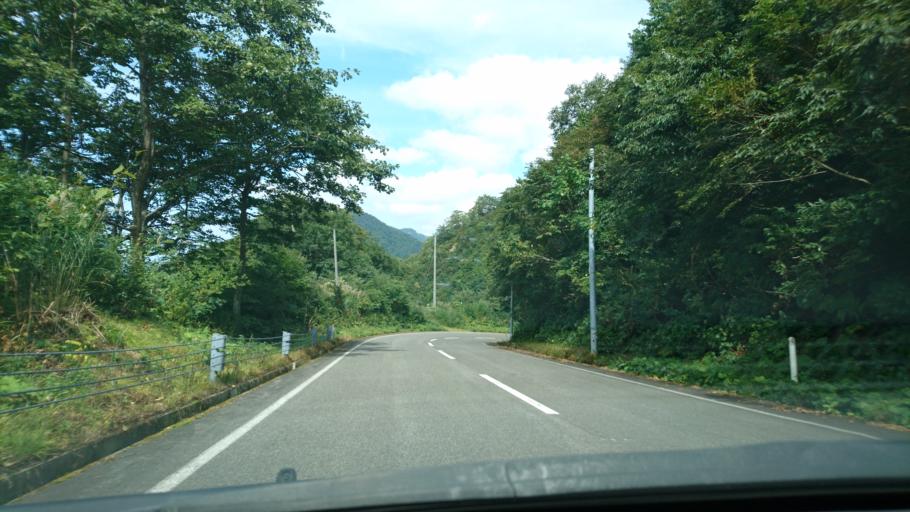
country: JP
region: Akita
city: Yuzawa
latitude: 39.0191
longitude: 140.7277
